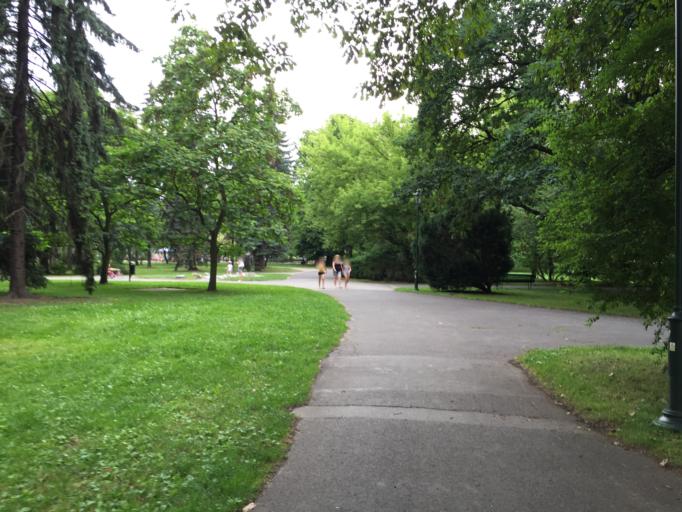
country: PL
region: Lesser Poland Voivodeship
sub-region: Krakow
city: Krakow
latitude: 50.0638
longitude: 19.9166
